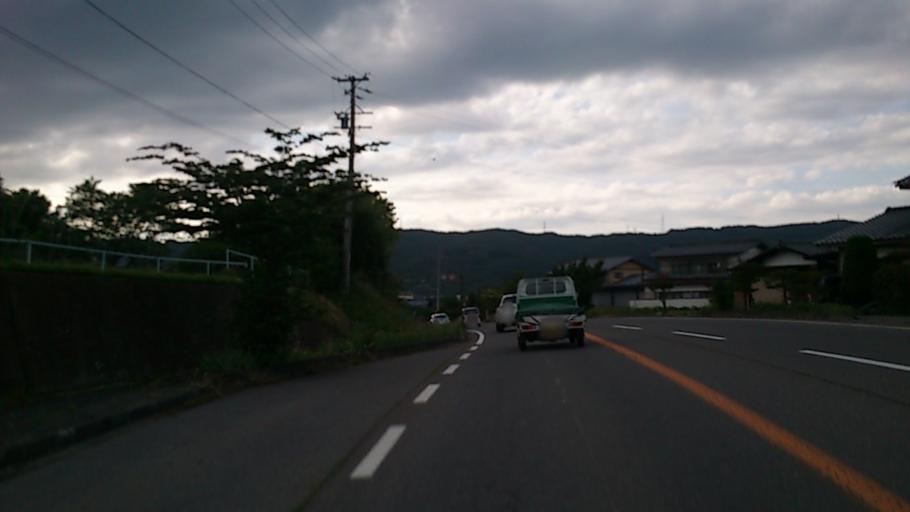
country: JP
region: Nagano
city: Komoro
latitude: 36.2675
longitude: 138.3981
